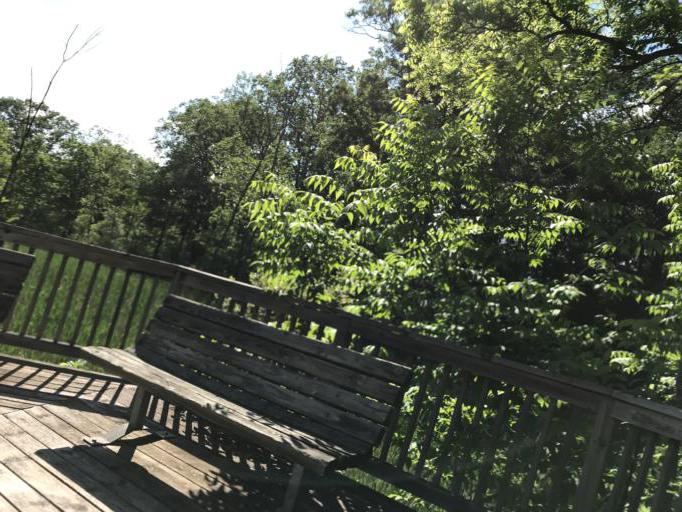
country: US
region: Michigan
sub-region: Oakland County
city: South Lyon
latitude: 42.4430
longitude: -83.6600
